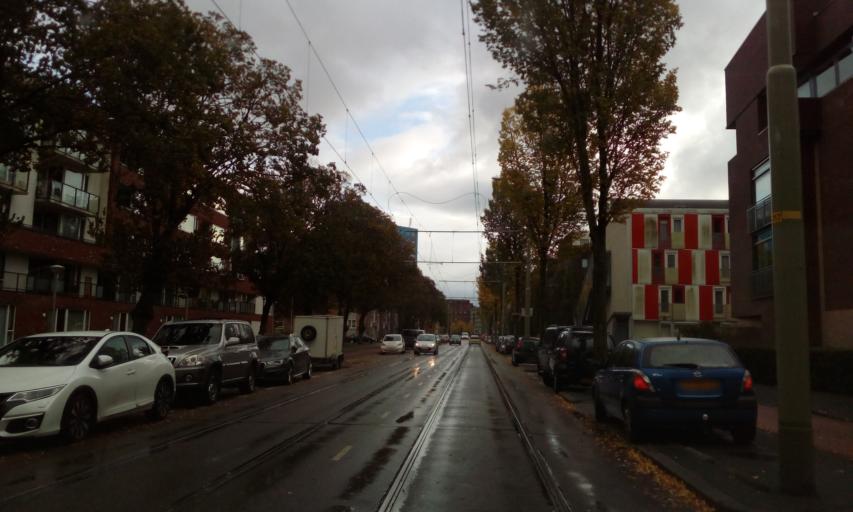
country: NL
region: South Holland
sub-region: Gemeente Westland
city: Kwintsheul
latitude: 52.0459
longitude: 4.2703
